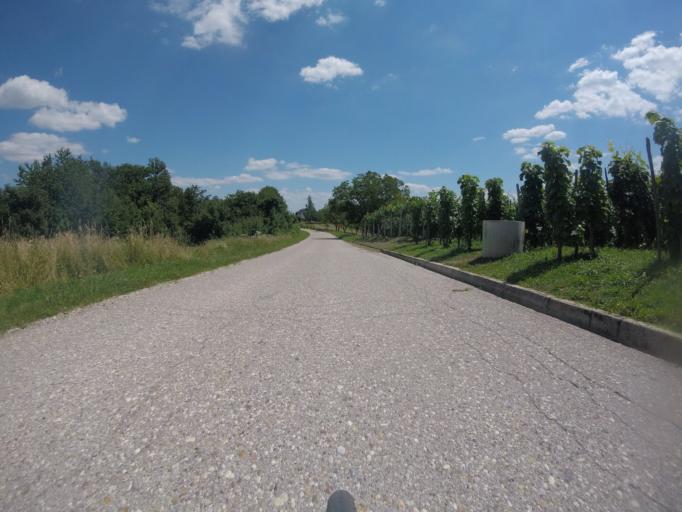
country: HR
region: Karlovacka
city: Ozalj
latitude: 45.6746
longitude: 15.4591
